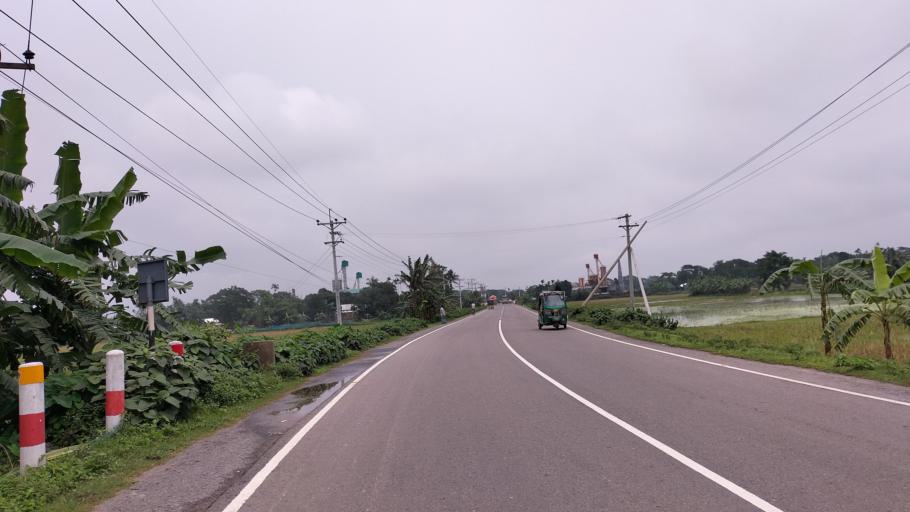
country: BD
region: Dhaka
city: Netrakona
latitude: 24.8527
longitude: 90.6510
